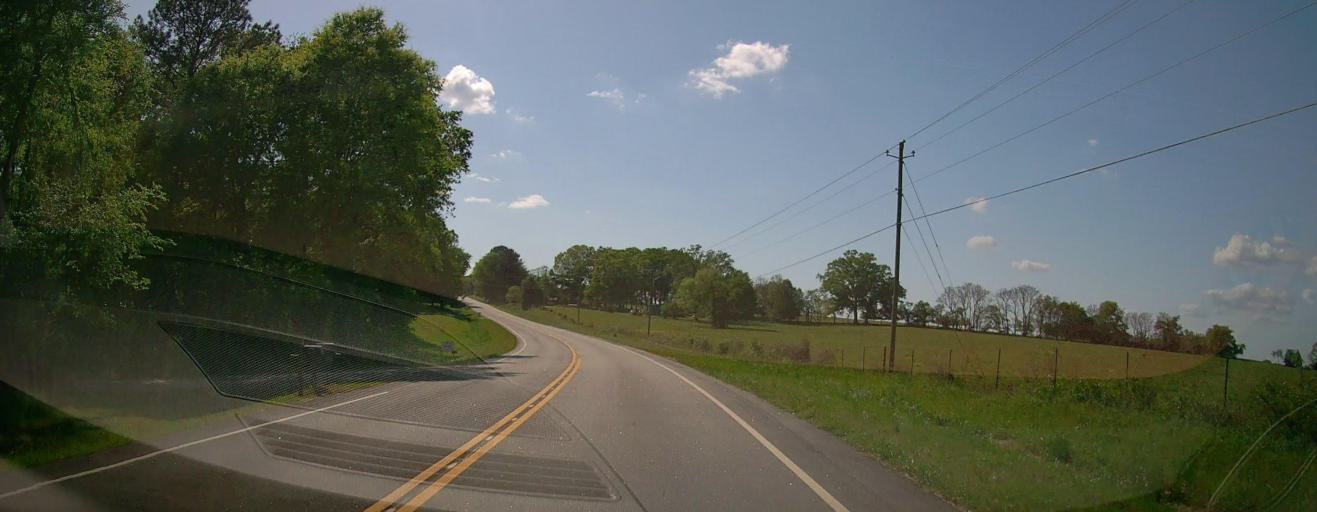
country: US
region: Georgia
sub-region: Morgan County
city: Madison
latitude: 33.6087
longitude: -83.3658
